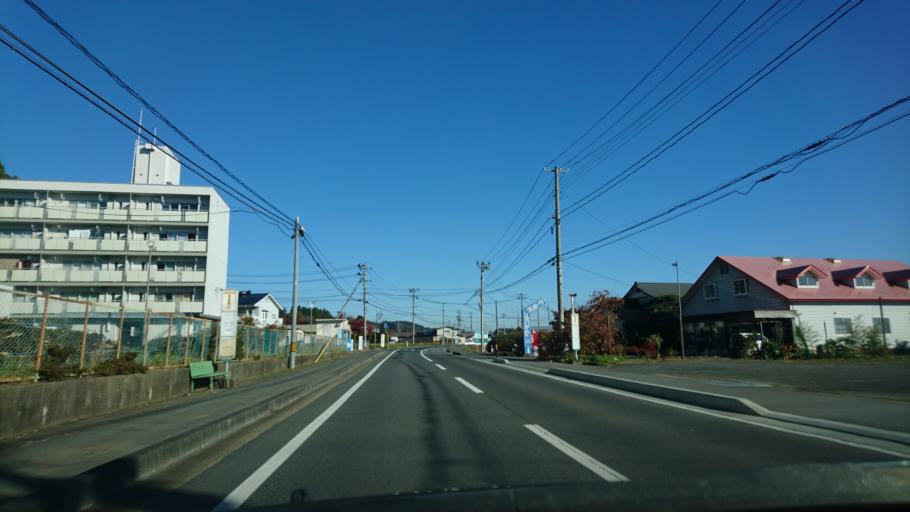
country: JP
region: Iwate
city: Mizusawa
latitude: 39.0633
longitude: 141.1258
